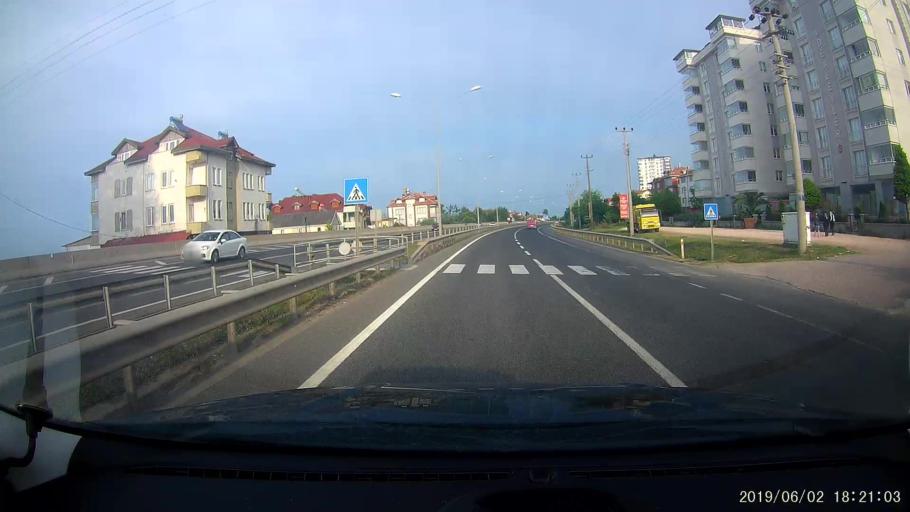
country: TR
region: Ordu
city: Fatsa
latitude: 41.0688
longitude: 37.4629
